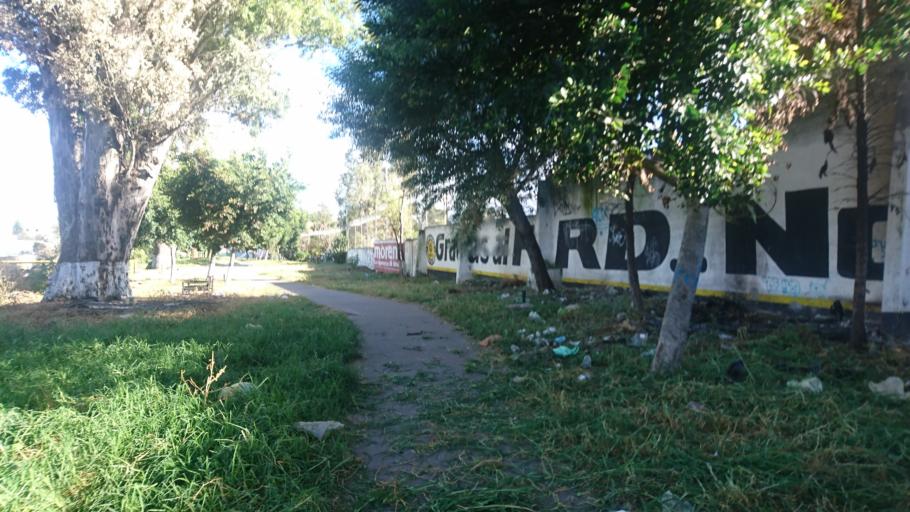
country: MX
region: Mexico City
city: Iztapalapa
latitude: 19.3247
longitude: -99.1043
